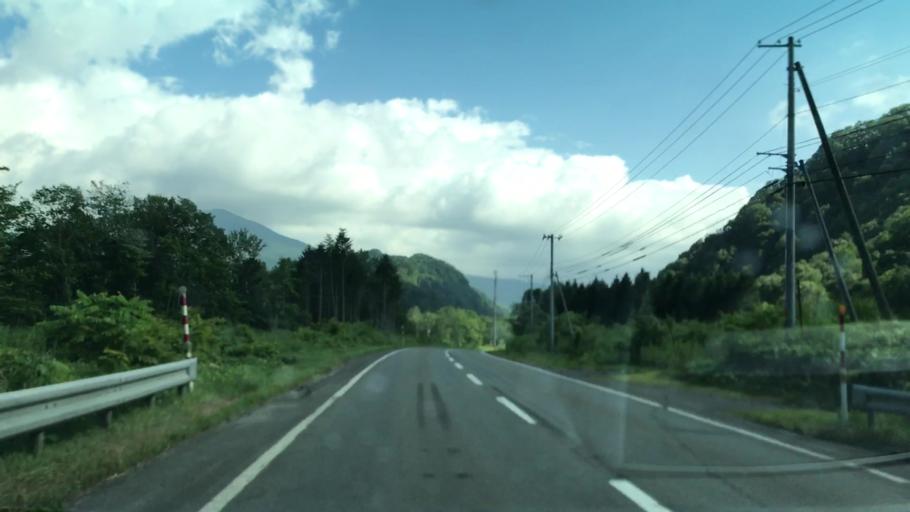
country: JP
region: Hokkaido
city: Shimo-furano
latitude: 42.8479
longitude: 142.4167
